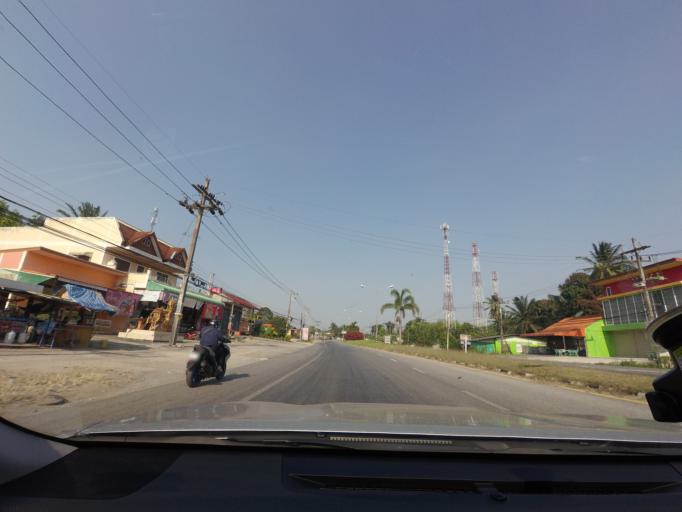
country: TH
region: Surat Thani
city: Chai Buri
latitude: 8.5684
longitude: 99.1169
